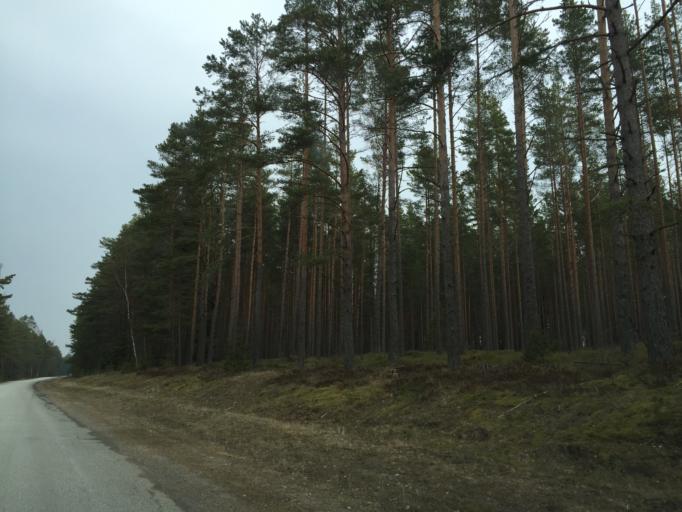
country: LV
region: Salacgrivas
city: Ainazi
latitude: 57.9747
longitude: 24.4122
